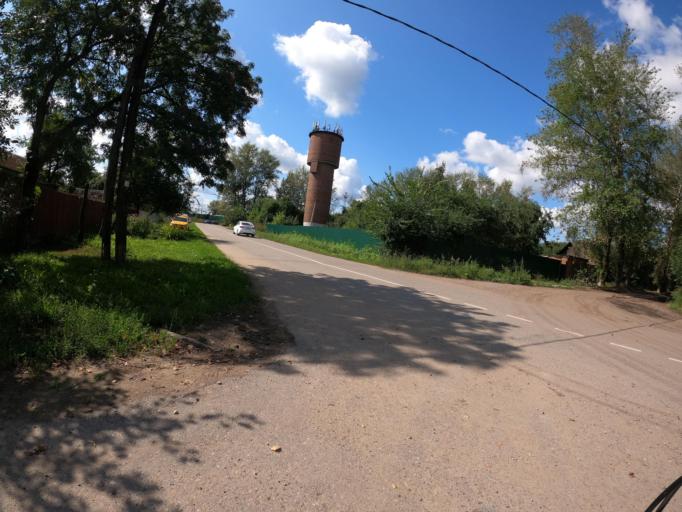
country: RU
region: Moskovskaya
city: Lopatinskiy
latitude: 55.3151
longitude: 38.7026
